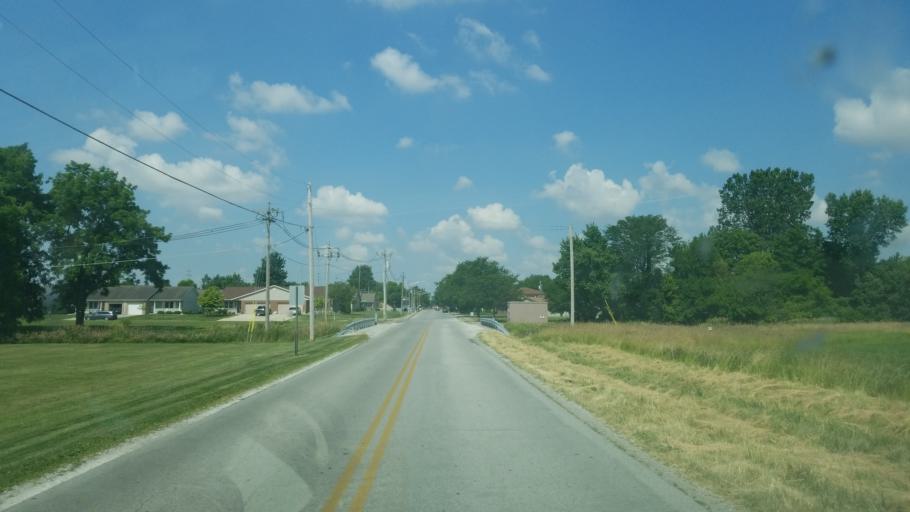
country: US
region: Ohio
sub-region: Auglaize County
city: Wapakoneta
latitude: 40.5700
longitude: -84.1751
